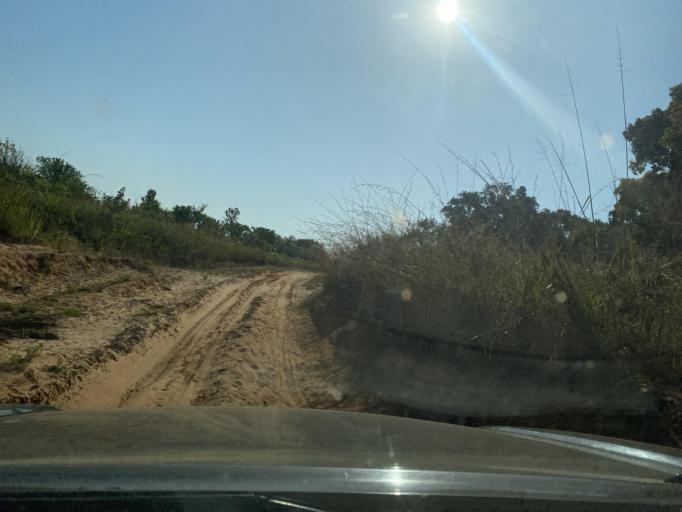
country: CD
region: Kasai-Oriental
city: Kabinda
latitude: -6.1162
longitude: 24.3569
